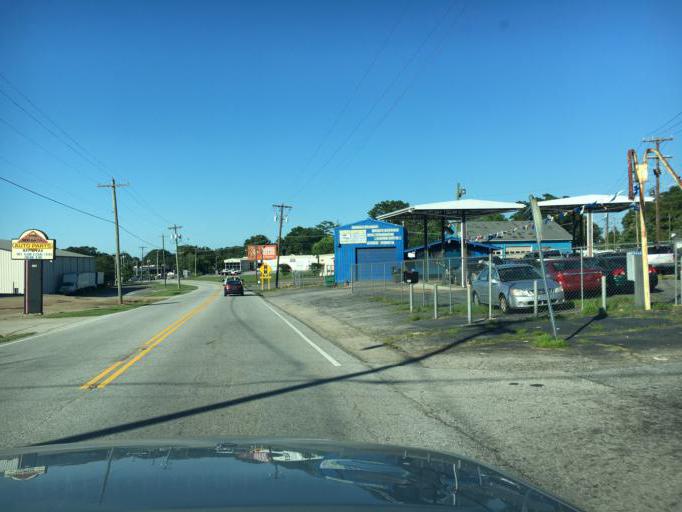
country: US
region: South Carolina
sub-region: Greenville County
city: Greer
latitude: 34.9452
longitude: -82.2165
